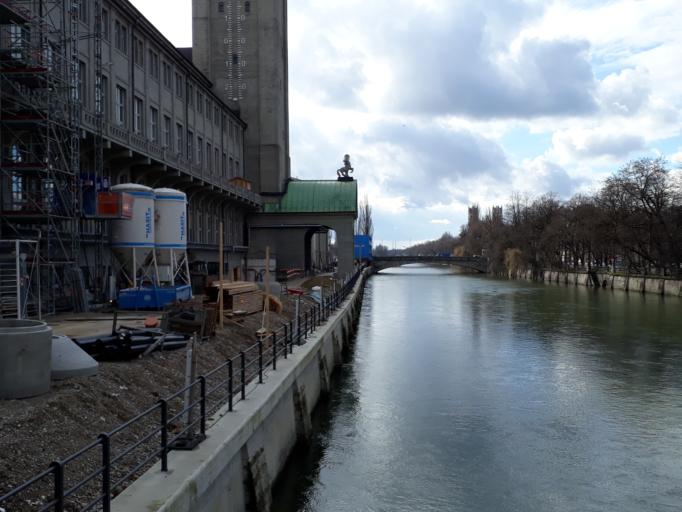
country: DE
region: Bavaria
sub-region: Upper Bavaria
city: Munich
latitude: 48.1304
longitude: 11.5829
